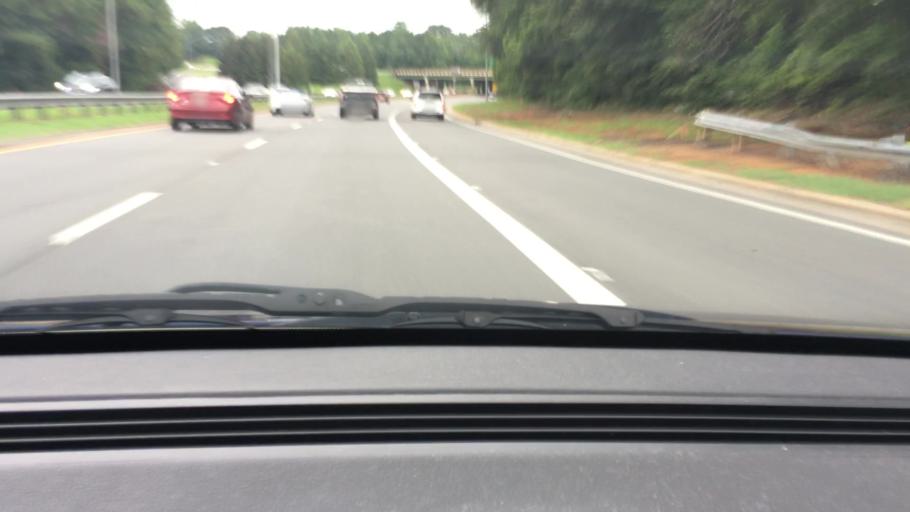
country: US
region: Alabama
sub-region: Tuscaloosa County
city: Tuscaloosa
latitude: 33.2175
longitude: -87.5304
